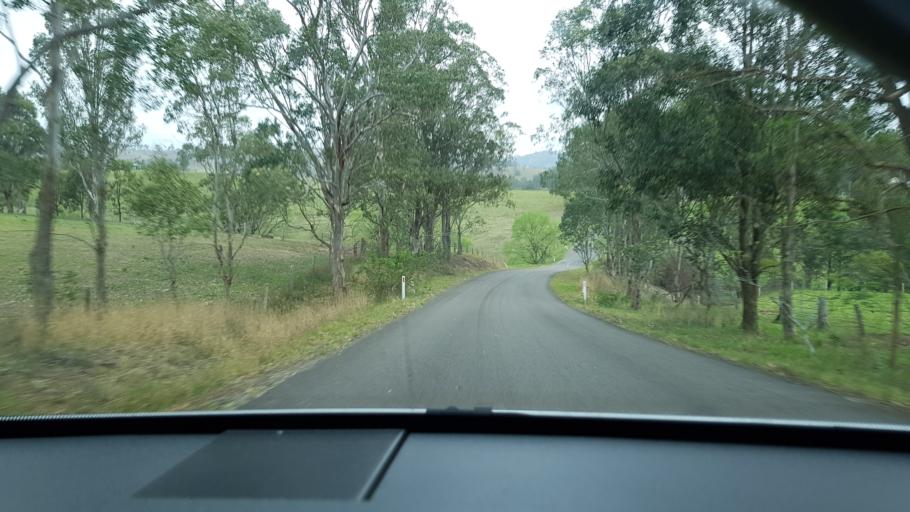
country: AU
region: New South Wales
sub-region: Dungog
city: Dungog
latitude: -32.2543
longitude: 151.6077
